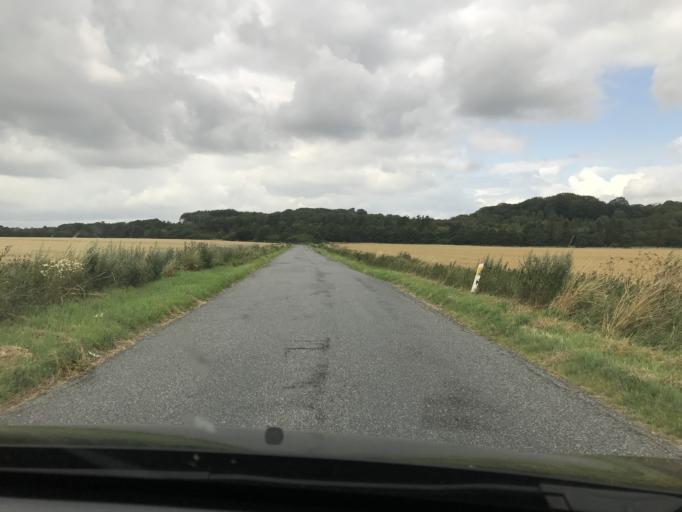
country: DK
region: Central Jutland
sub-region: Norddjurs Kommune
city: Auning
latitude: 56.3837
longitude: 10.4306
